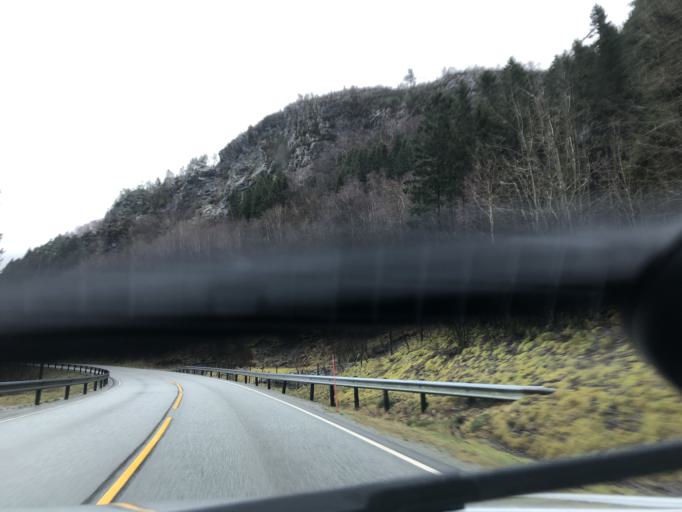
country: NO
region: Rogaland
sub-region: Hjelmeland
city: Hjelmelandsvagen
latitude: 59.2194
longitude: 6.1356
